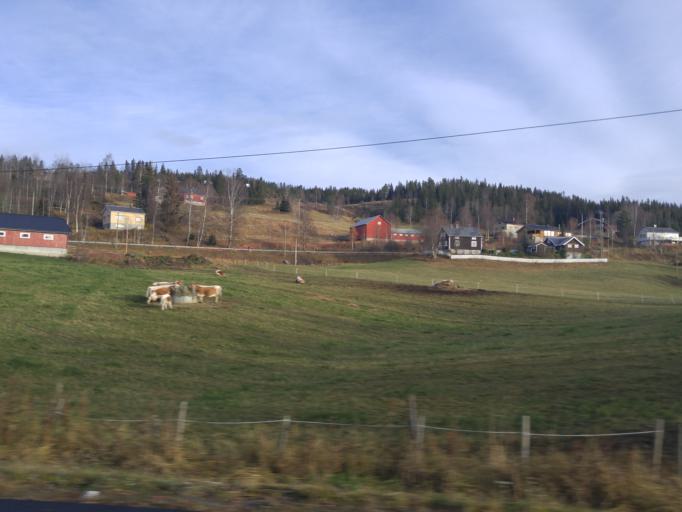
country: NO
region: Oppland
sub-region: Nord-Aurdal
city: Fagernes
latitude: 61.0607
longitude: 9.1651
